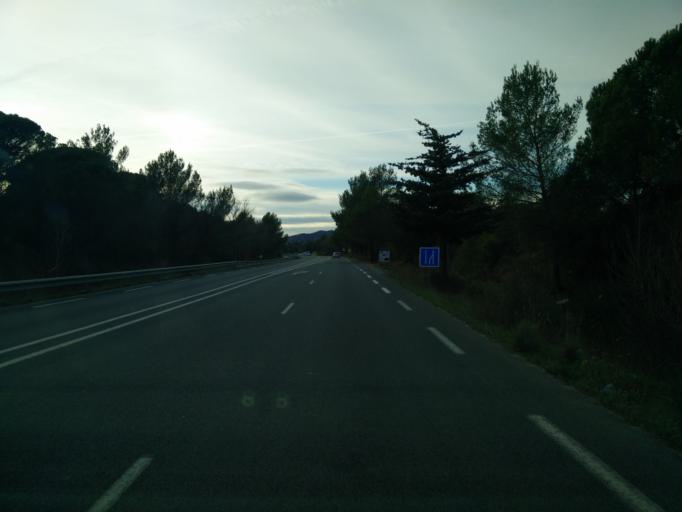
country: FR
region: Provence-Alpes-Cote d'Azur
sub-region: Departement du Var
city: La Londe-les-Maures
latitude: 43.1479
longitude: 6.2661
